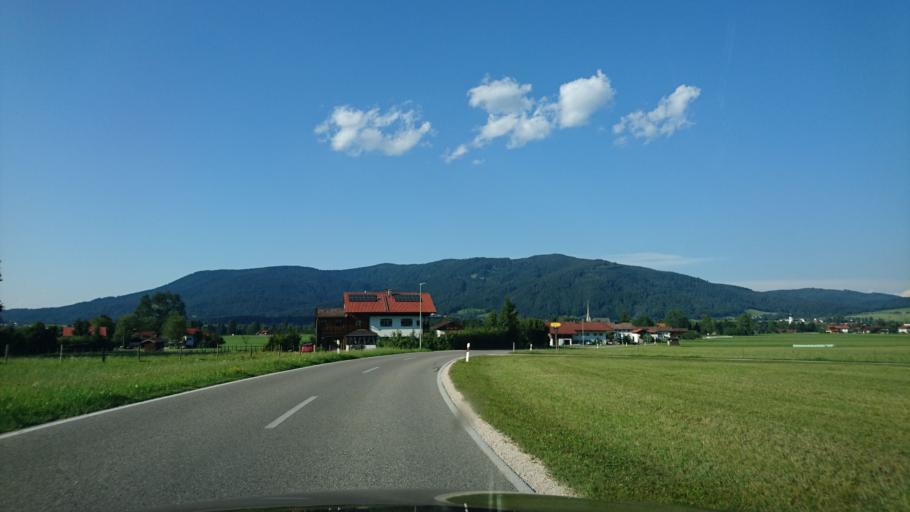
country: DE
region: Bavaria
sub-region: Upper Bavaria
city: Inzell
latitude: 47.7565
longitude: 12.7309
